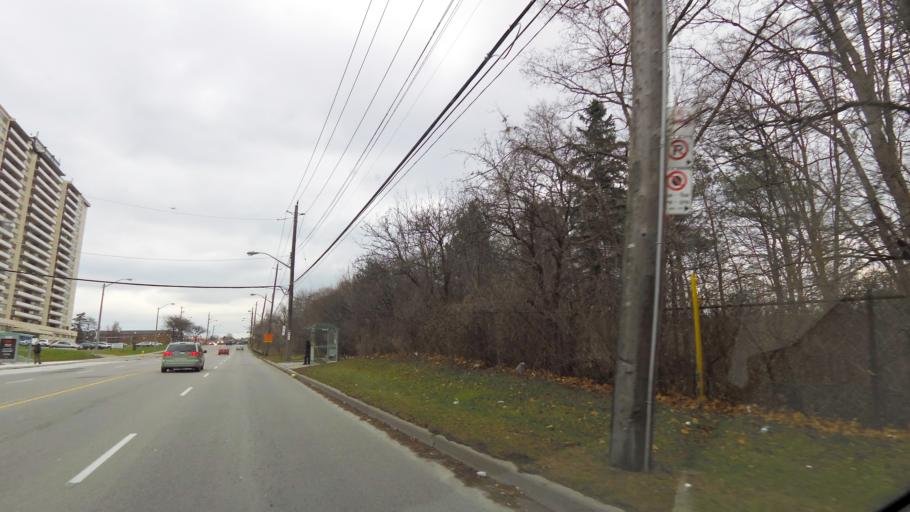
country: CA
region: Ontario
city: Concord
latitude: 43.7384
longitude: -79.5173
